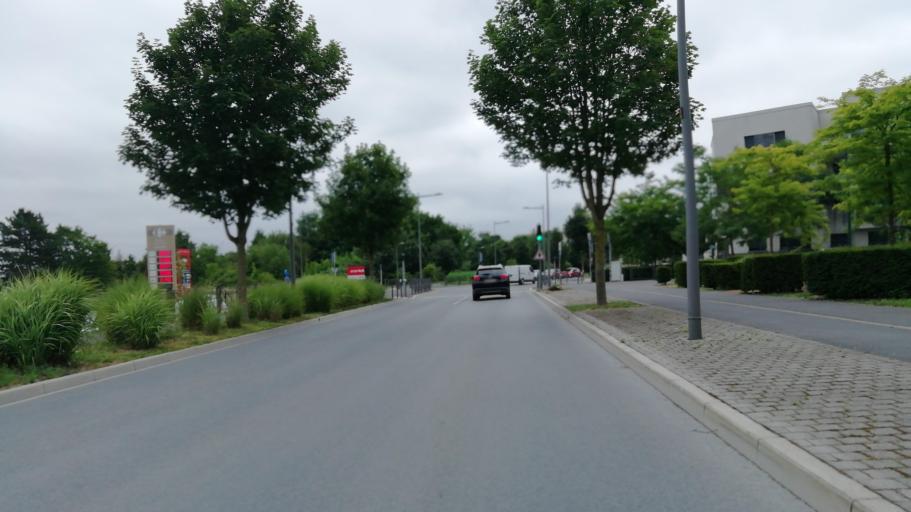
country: FR
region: Champagne-Ardenne
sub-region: Departement de la Marne
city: Betheny
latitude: 49.2590
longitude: 4.0631
